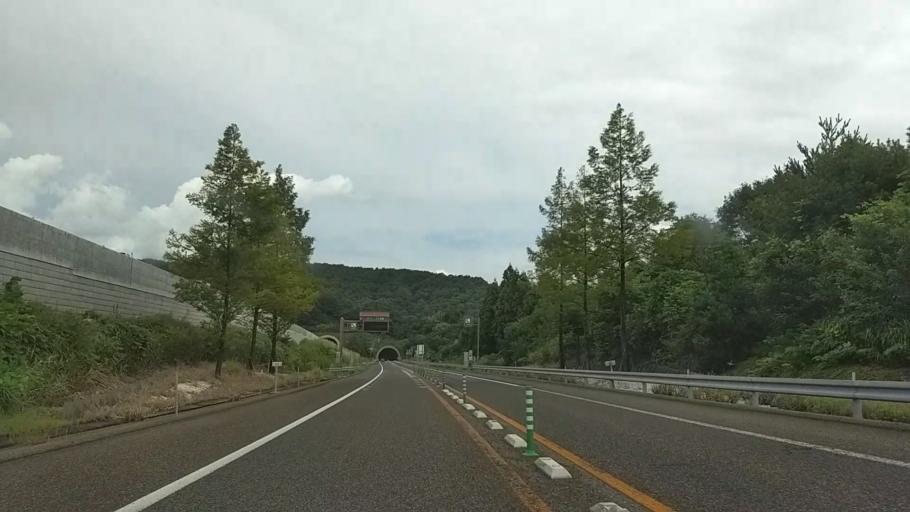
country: JP
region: Niigata
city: Arai
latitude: 37.0395
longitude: 138.2321
